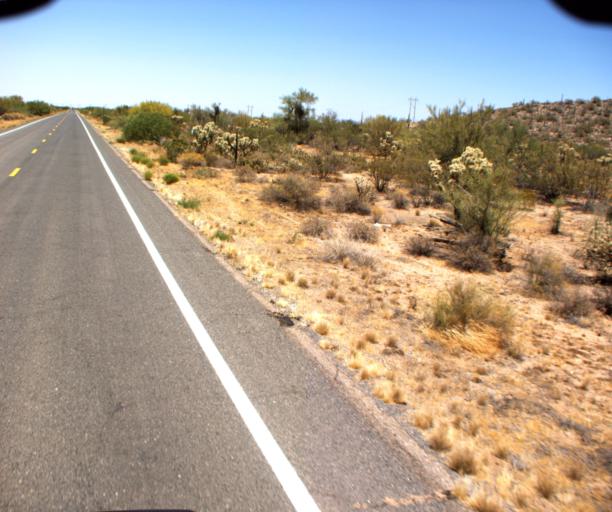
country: US
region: Arizona
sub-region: Pinal County
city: Florence
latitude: 32.7827
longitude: -111.1680
